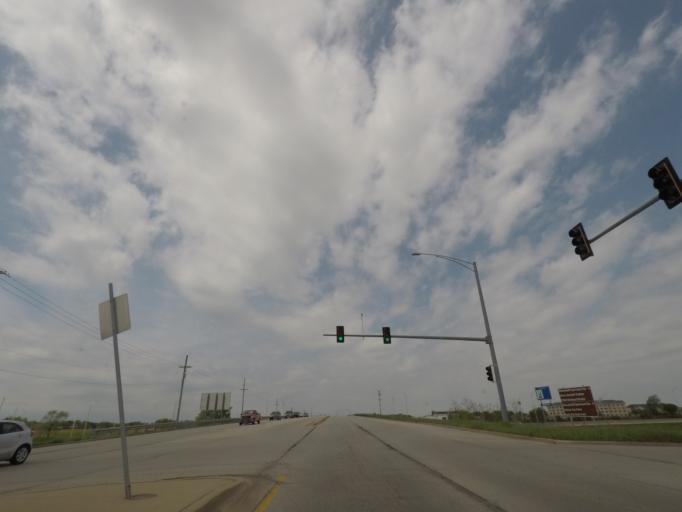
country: US
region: Illinois
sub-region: Winnebago County
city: Machesney Park
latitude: 42.3191
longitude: -88.9624
